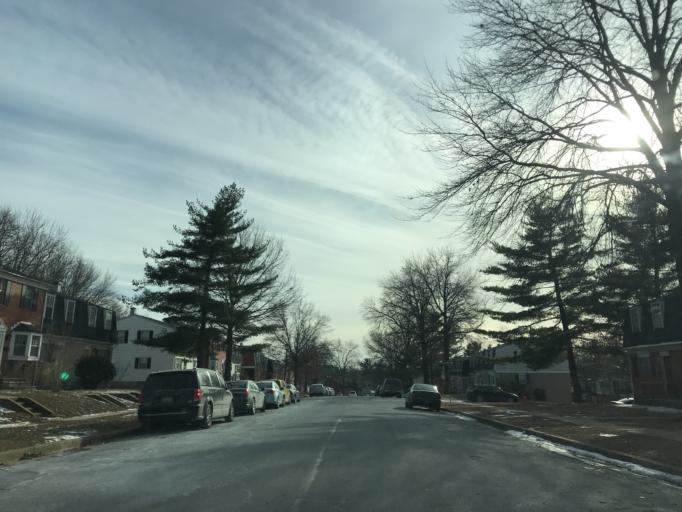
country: US
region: Maryland
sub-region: Baltimore County
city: Rosedale
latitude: 39.3296
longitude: -76.5265
